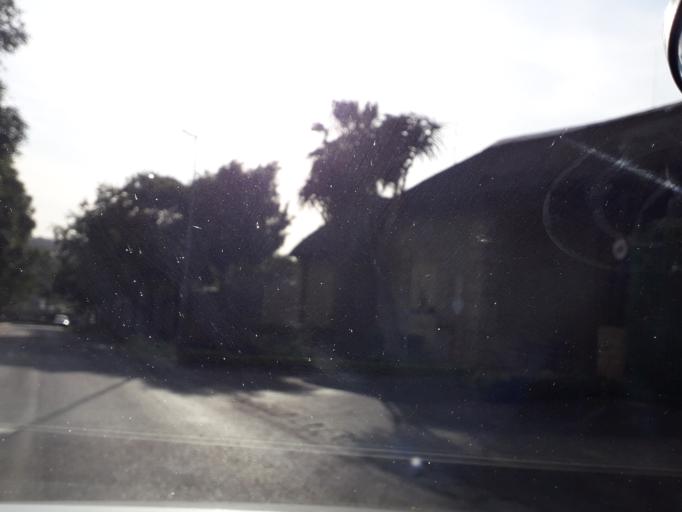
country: ZA
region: Gauteng
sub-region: City of Johannesburg Metropolitan Municipality
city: Diepsloot
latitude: -26.0452
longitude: 27.9909
